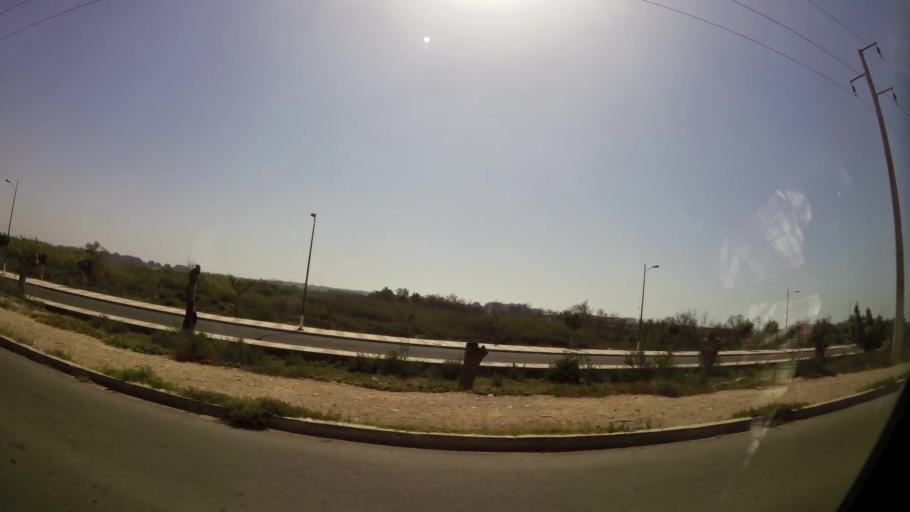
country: MA
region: Souss-Massa-Draa
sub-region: Inezgane-Ait Mellou
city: Inezgane
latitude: 30.3588
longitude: -9.5662
